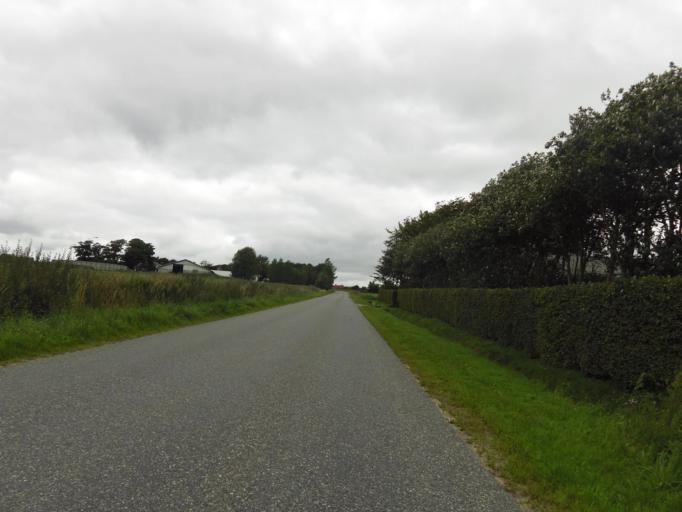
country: DK
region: South Denmark
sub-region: Haderslev Kommune
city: Gram
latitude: 55.2649
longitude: 9.1665
